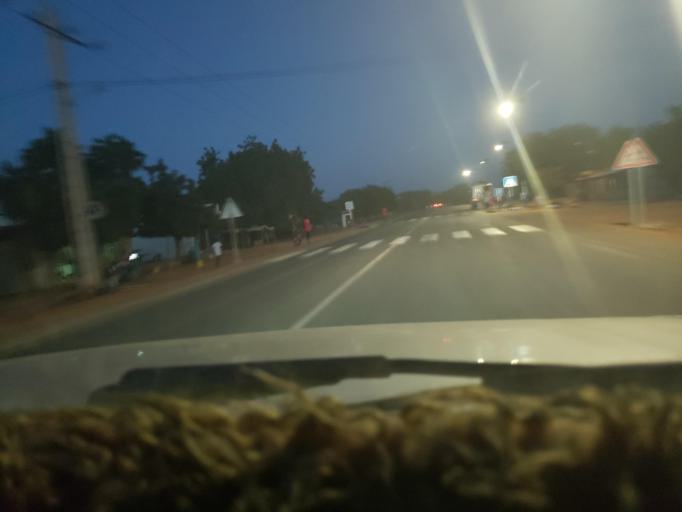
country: SN
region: Louga
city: Ndibene Dahra
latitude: 15.3846
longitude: -15.2371
